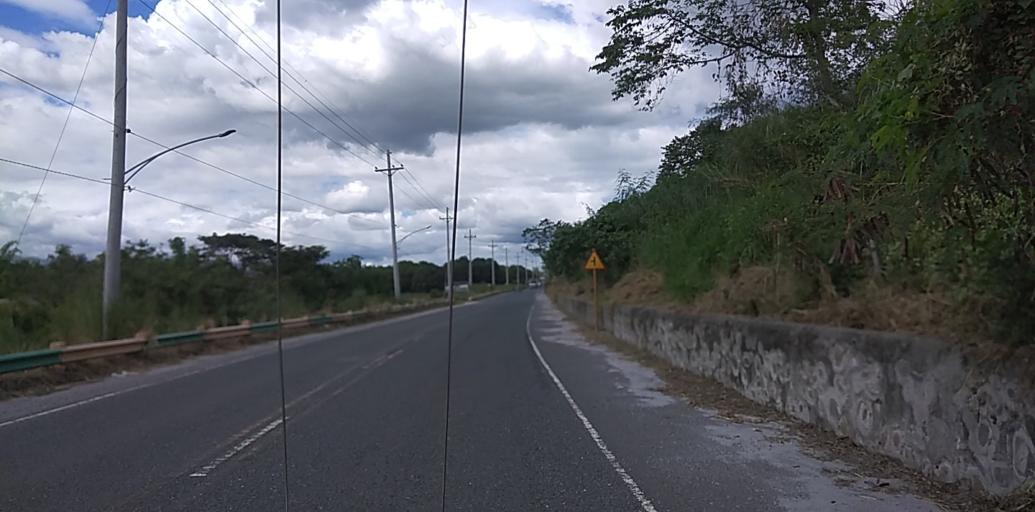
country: PH
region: Central Luzon
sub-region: Province of Pampanga
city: Dolores
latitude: 15.0992
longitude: 120.5251
